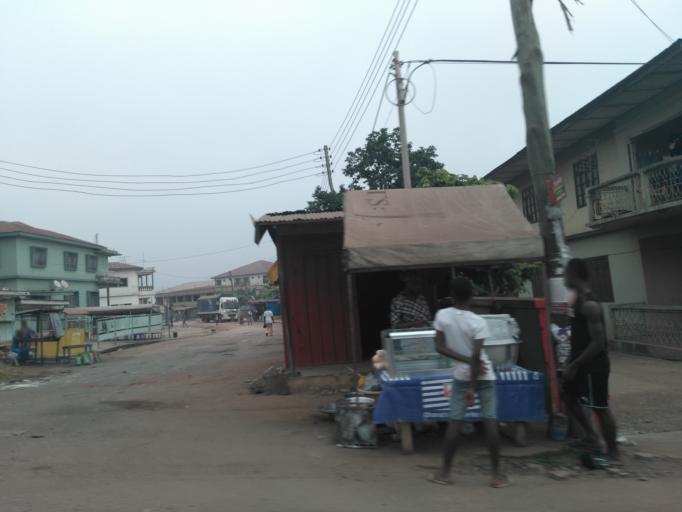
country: GH
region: Ashanti
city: Tafo
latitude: 6.7142
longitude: -1.6049
